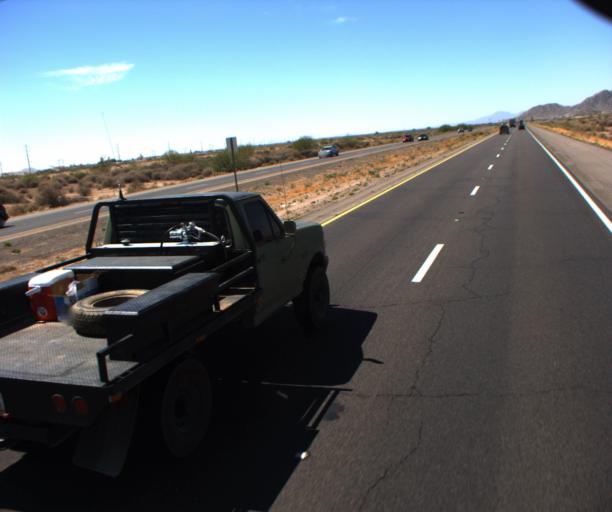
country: US
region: Arizona
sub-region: Maricopa County
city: Sun Lakes
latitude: 33.1871
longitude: -111.9996
